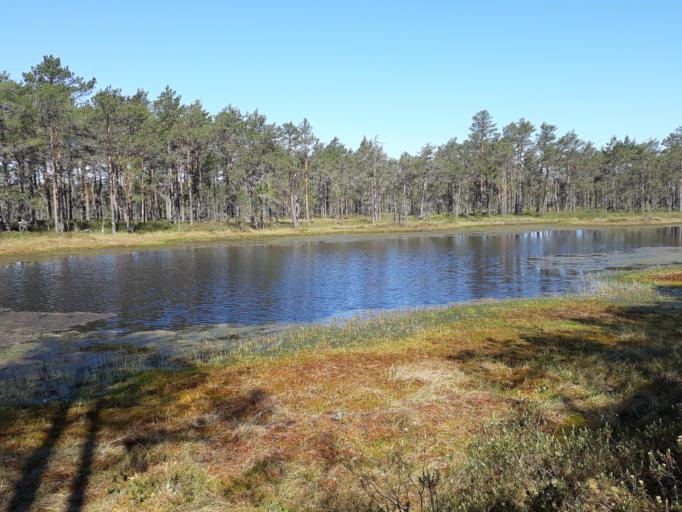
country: EE
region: Harju
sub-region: Loksa linn
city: Loksa
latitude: 59.4729
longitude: 25.6635
